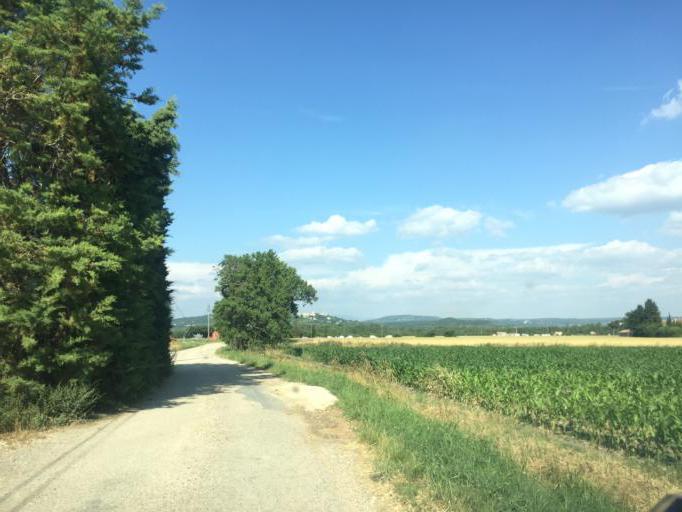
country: FR
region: Rhone-Alpes
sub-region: Departement de la Drome
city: Pierrelatte
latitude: 44.3840
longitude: 4.7143
